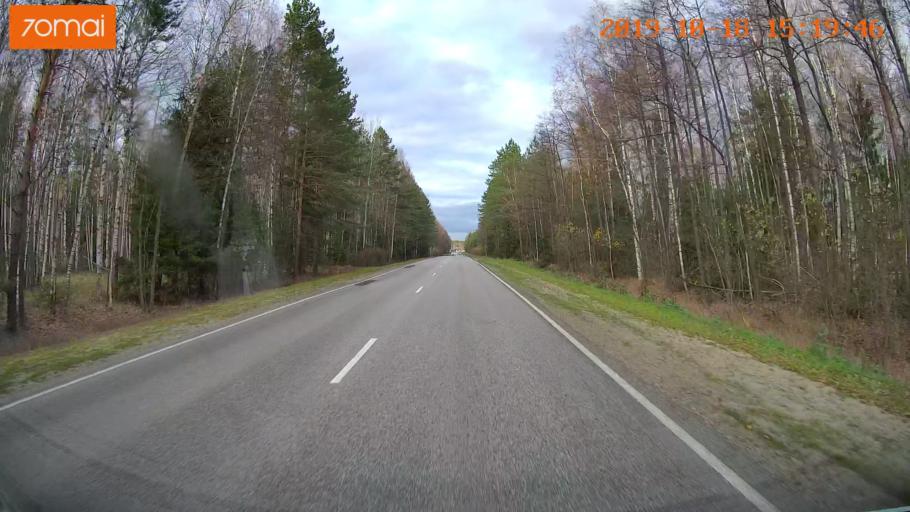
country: RU
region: Vladimir
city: Anopino
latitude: 55.6779
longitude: 40.7401
